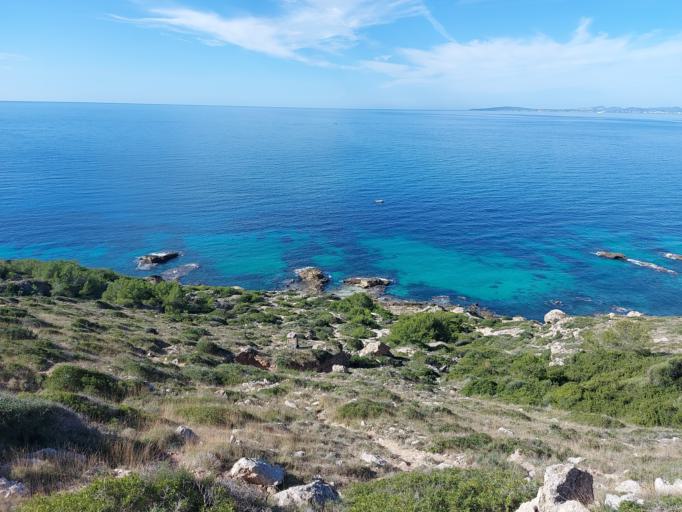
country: ES
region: Balearic Islands
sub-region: Illes Balears
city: s'Arenal
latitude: 39.4407
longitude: 2.7497
